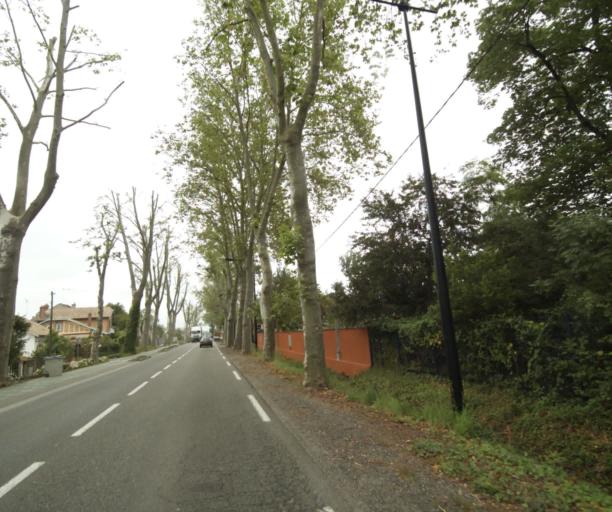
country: FR
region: Midi-Pyrenees
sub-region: Departement du Tarn-et-Garonne
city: Montauban
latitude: 43.9993
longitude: 1.3395
